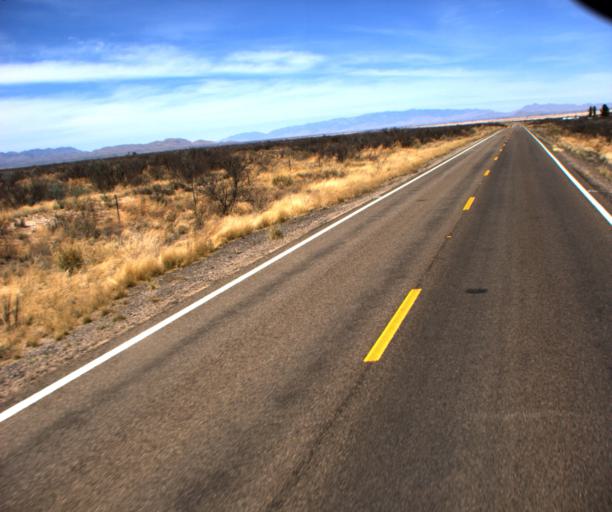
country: US
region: Arizona
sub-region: Cochise County
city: Willcox
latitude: 32.1160
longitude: -109.9118
